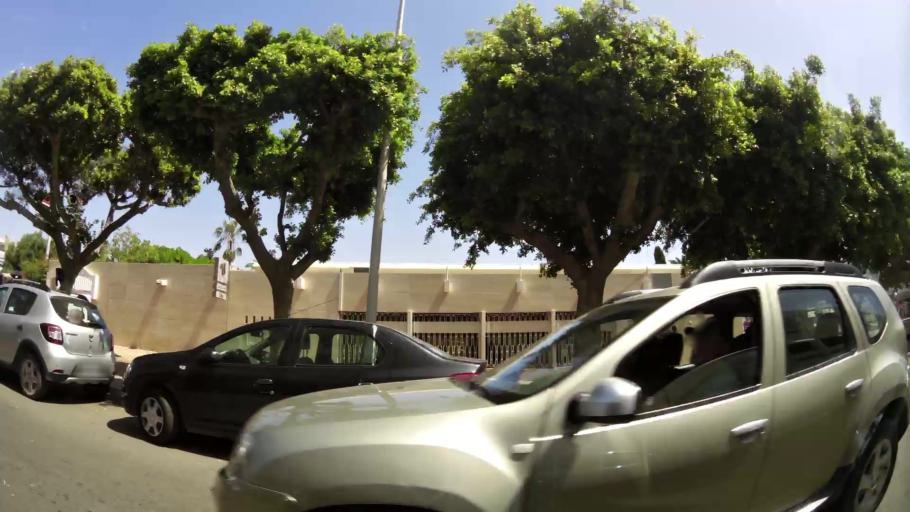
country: MA
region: Souss-Massa-Draa
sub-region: Agadir-Ida-ou-Tnan
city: Agadir
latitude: 30.4236
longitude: -9.6029
